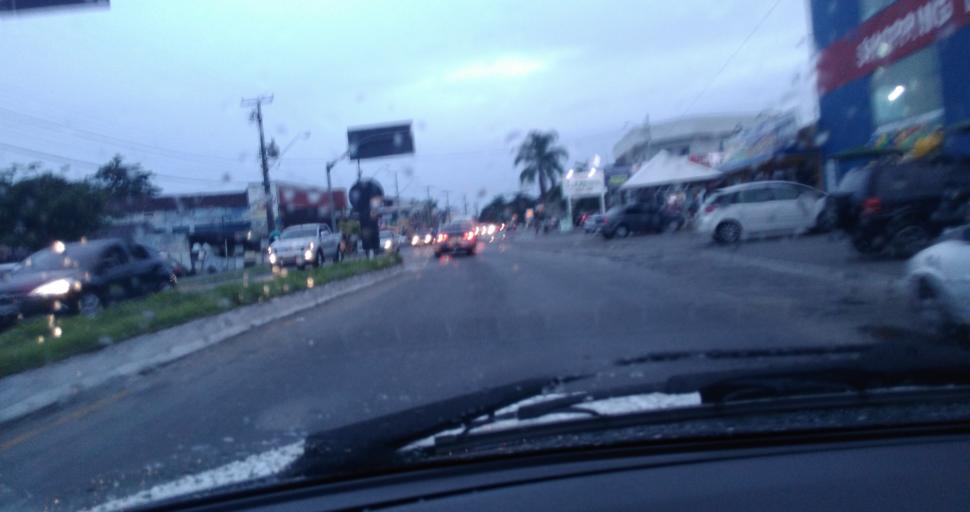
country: BR
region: Parana
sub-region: Guaratuba
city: Guaratuba
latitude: -25.8102
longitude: -48.5328
